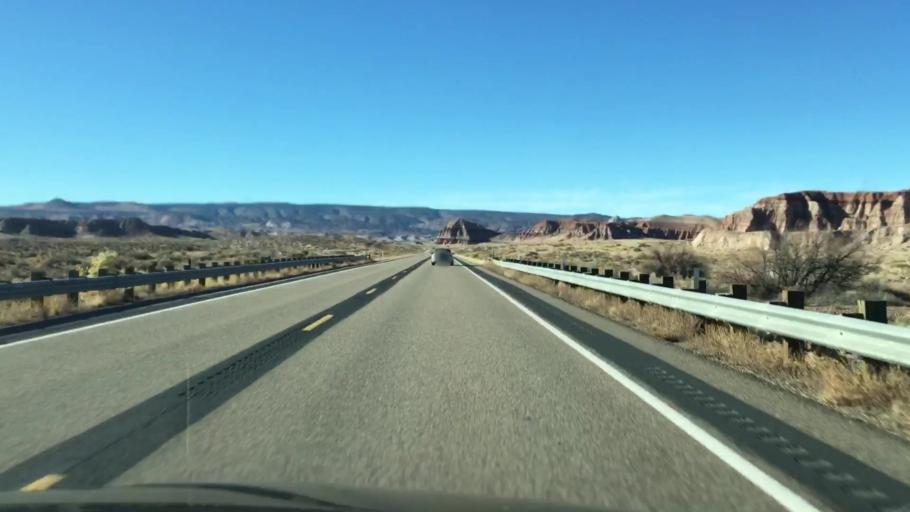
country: US
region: Arizona
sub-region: Coconino County
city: Page
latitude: 37.1034
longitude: -111.8826
